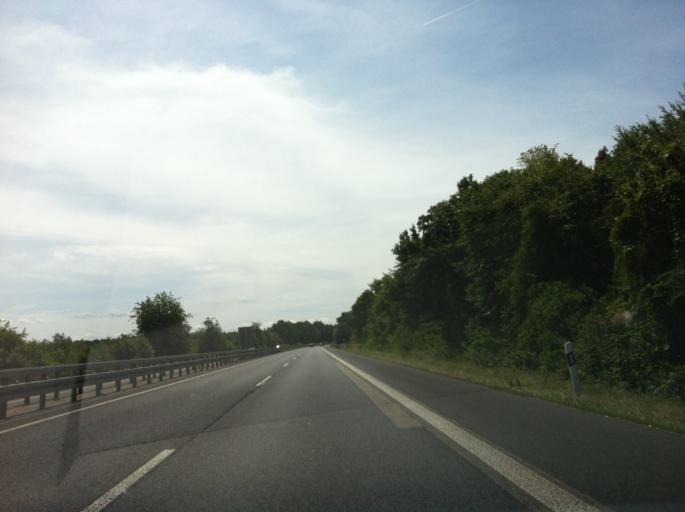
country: DE
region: Hesse
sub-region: Regierungsbezirk Darmstadt
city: Rodgau
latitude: 50.0104
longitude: 8.8970
